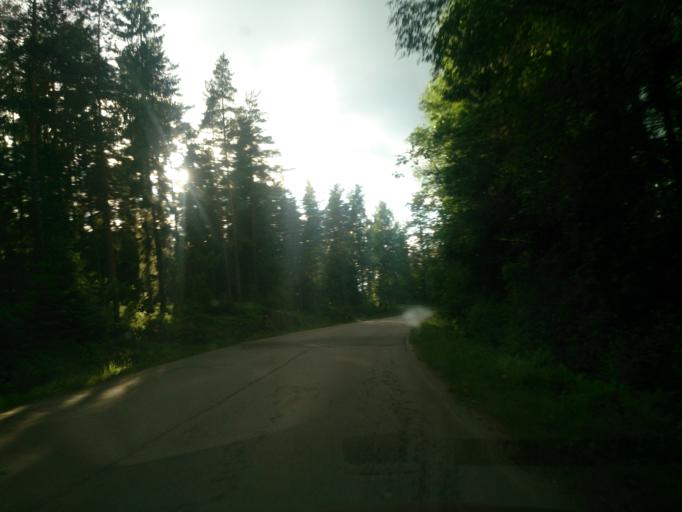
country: SE
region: OEstergoetland
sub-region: Norrkopings Kommun
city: Jursla
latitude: 58.7203
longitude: 16.1360
